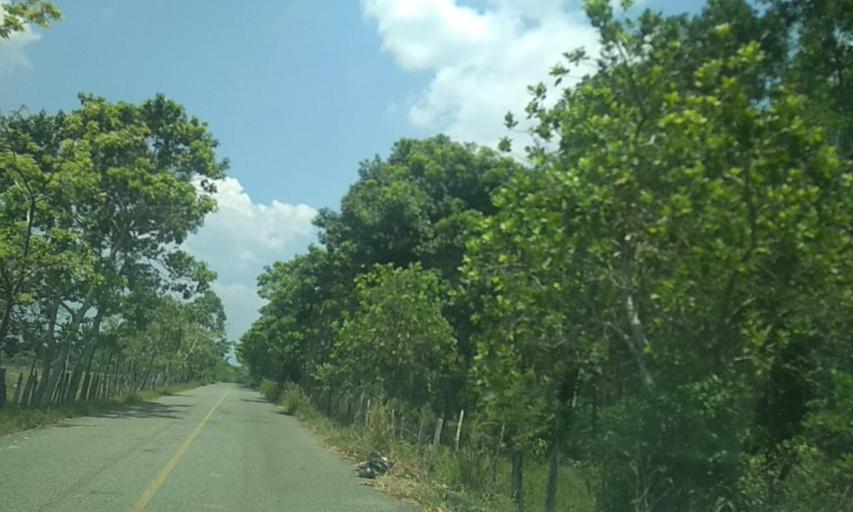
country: MX
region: Tabasco
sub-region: Huimanguillo
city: Francisco Rueda
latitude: 17.8369
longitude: -93.9123
